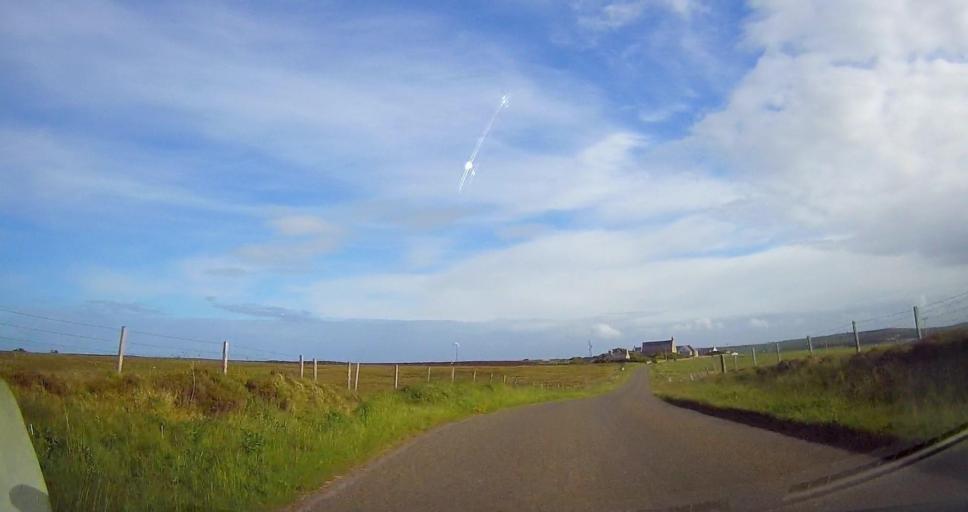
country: GB
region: Scotland
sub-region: Orkney Islands
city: Stromness
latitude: 58.8210
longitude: -3.2044
